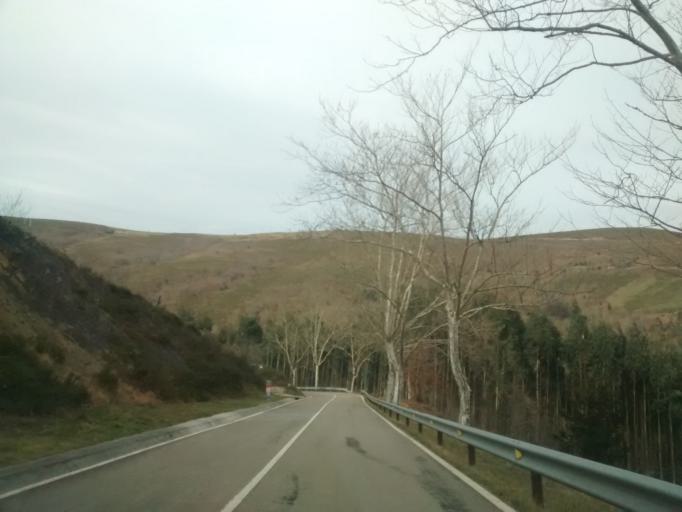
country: ES
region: Cantabria
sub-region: Provincia de Cantabria
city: Ruente
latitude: 43.2347
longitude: -4.3046
